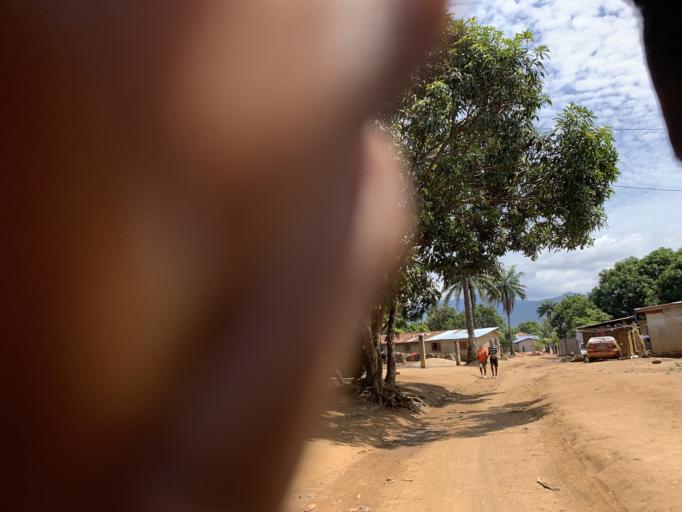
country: SL
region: Western Area
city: Waterloo
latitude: 8.3396
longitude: -13.0508
